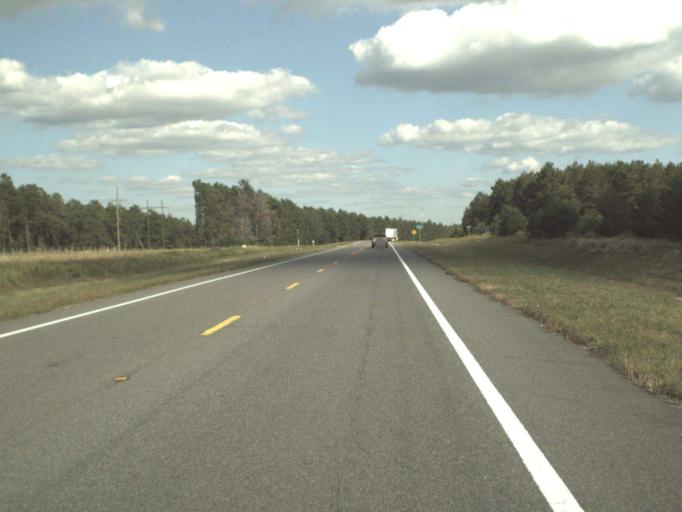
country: US
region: Florida
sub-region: Bay County
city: Lynn Haven
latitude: 30.4389
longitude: -85.7080
